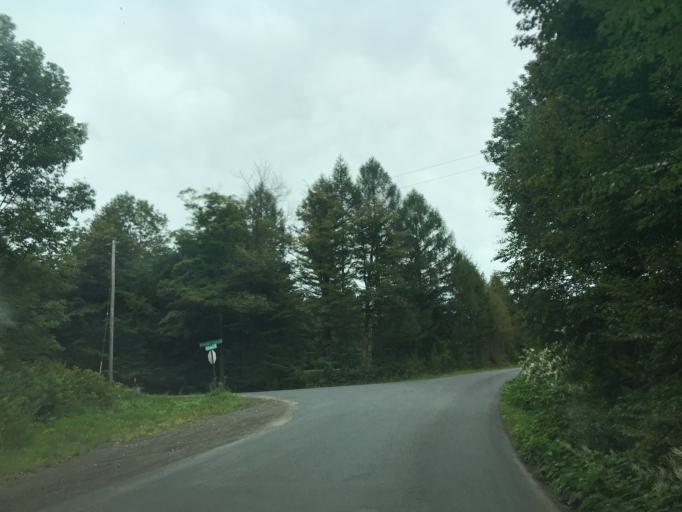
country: US
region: New York
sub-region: Otsego County
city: Worcester
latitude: 42.5896
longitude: -74.6998
